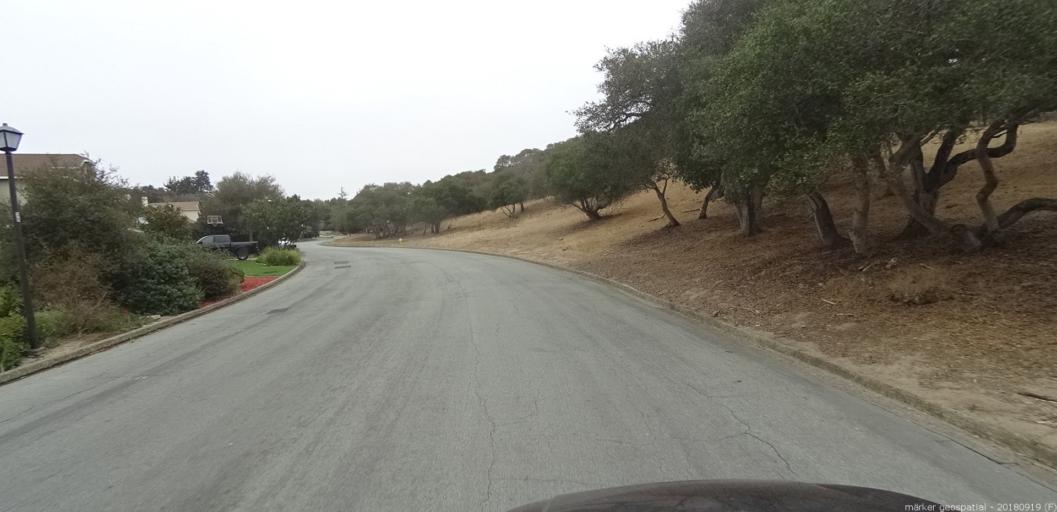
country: US
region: California
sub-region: Monterey County
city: Castroville
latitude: 36.7785
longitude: -121.7149
